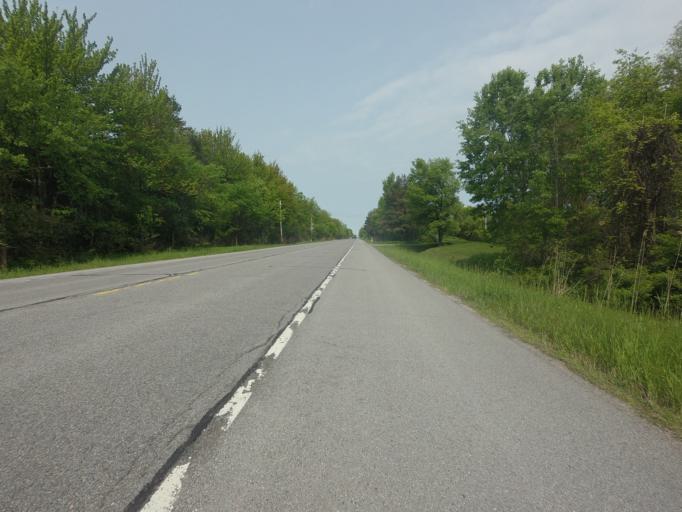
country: US
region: New York
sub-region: Jefferson County
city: Dexter
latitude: 44.0154
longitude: -76.0238
